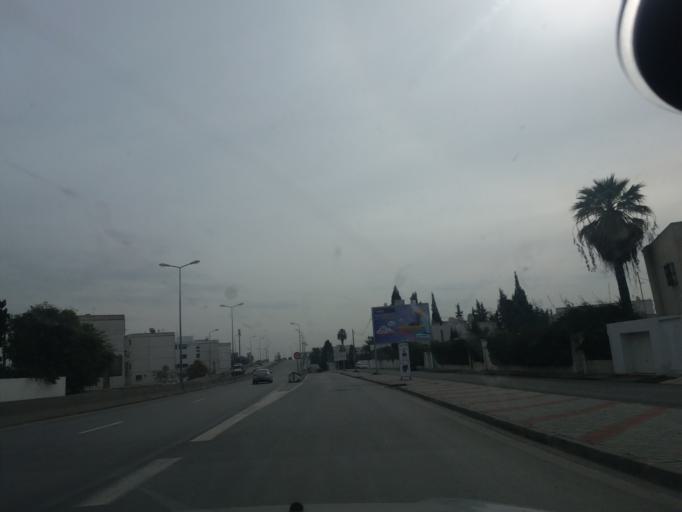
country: TN
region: Tunis
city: Tunis
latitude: 36.8340
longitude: 10.1775
